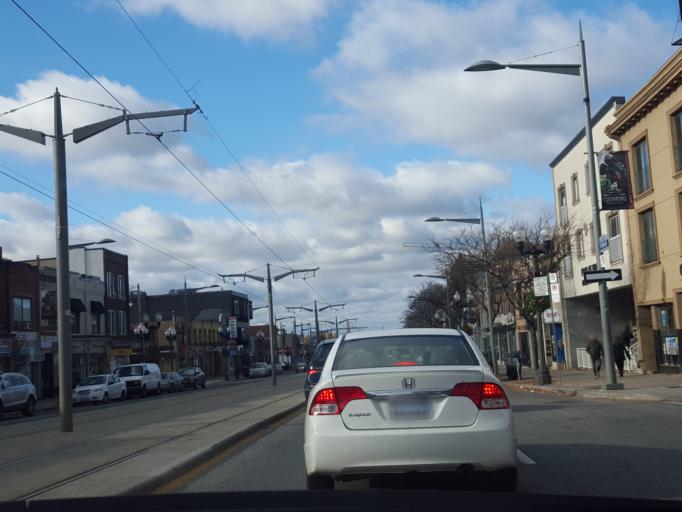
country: CA
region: Ontario
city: Toronto
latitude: 43.6768
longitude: -79.4485
